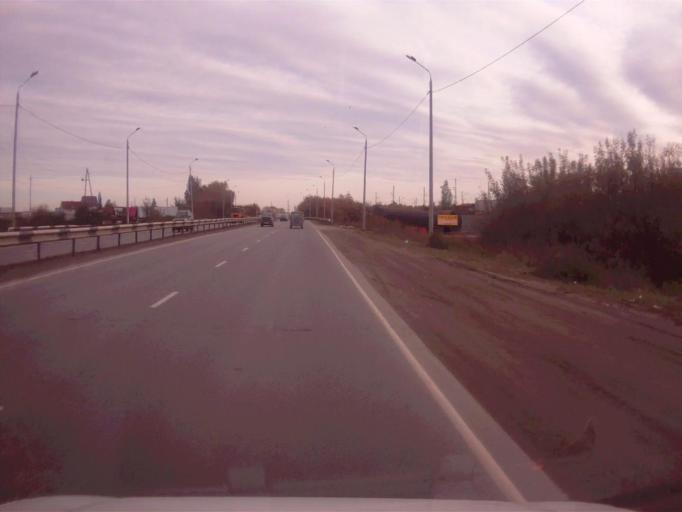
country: RU
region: Chelyabinsk
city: Novosineglazovskiy
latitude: 55.0445
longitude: 61.4220
